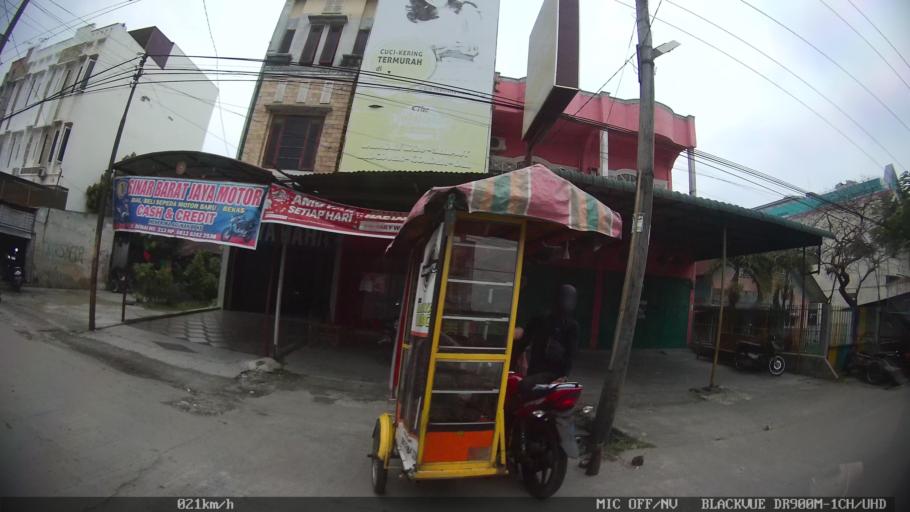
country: ID
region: North Sumatra
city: Medan
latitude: 3.5816
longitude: 98.7201
